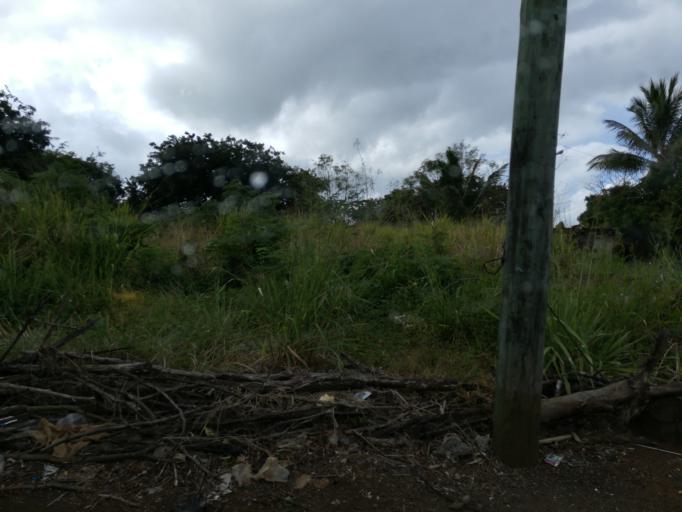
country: MU
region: Pamplemousses
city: Arsenal
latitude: -20.1000
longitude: 57.5411
